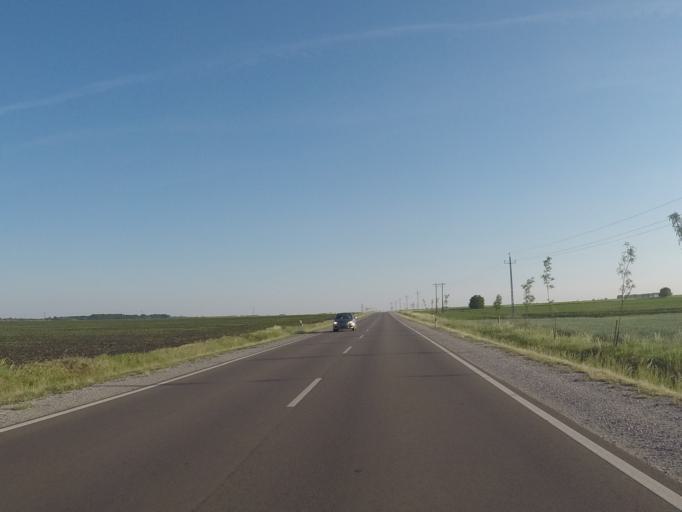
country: HU
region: Heves
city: Besenyotelek
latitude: 47.7108
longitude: 20.4100
